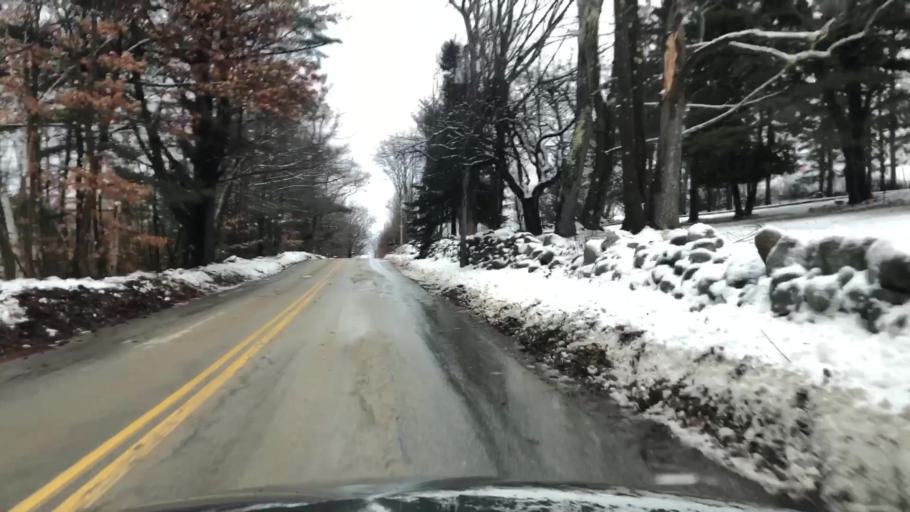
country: US
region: New Hampshire
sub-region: Hillsborough County
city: Mont Vernon
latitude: 42.9370
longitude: -71.6134
